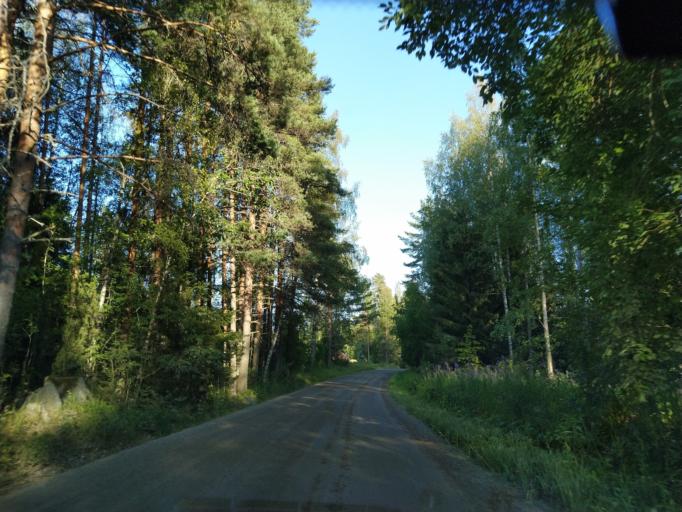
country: FI
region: Central Finland
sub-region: Jaemsae
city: Kuhmoinen
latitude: 61.6028
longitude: 25.1483
